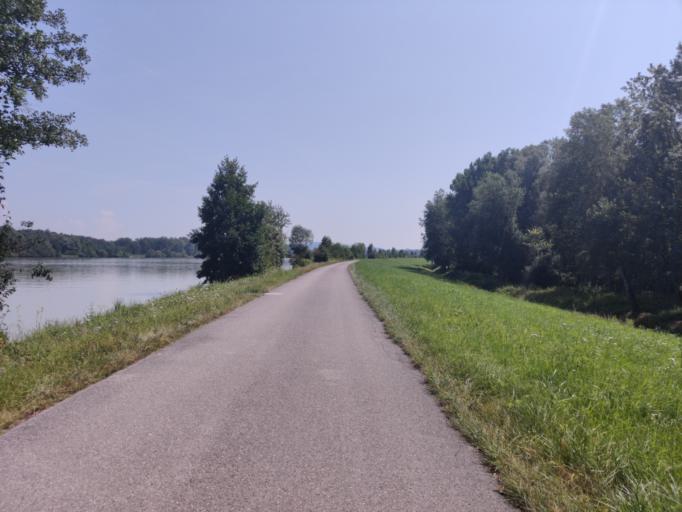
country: AT
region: Upper Austria
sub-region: Politischer Bezirk Urfahr-Umgebung
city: Goldworth
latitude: 48.3139
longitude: 14.0938
